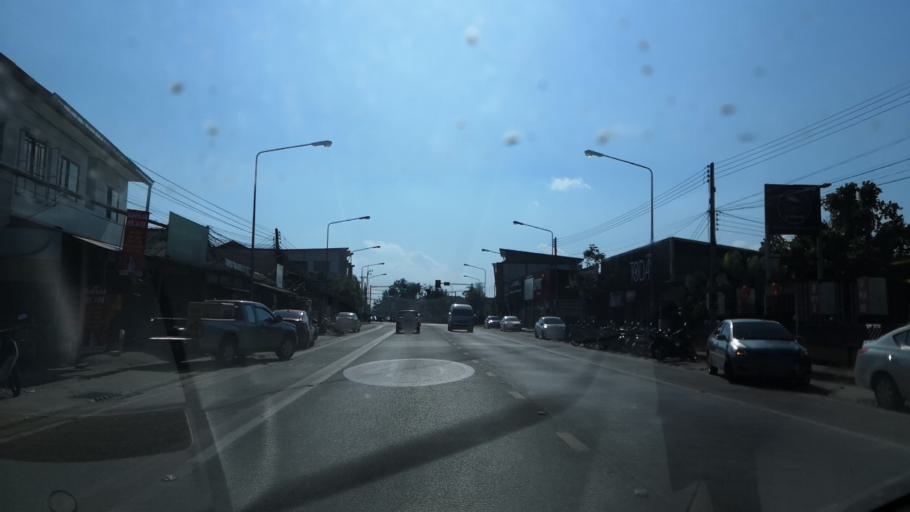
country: TH
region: Chiang Rai
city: Chiang Rai
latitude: 19.9346
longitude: 99.8420
